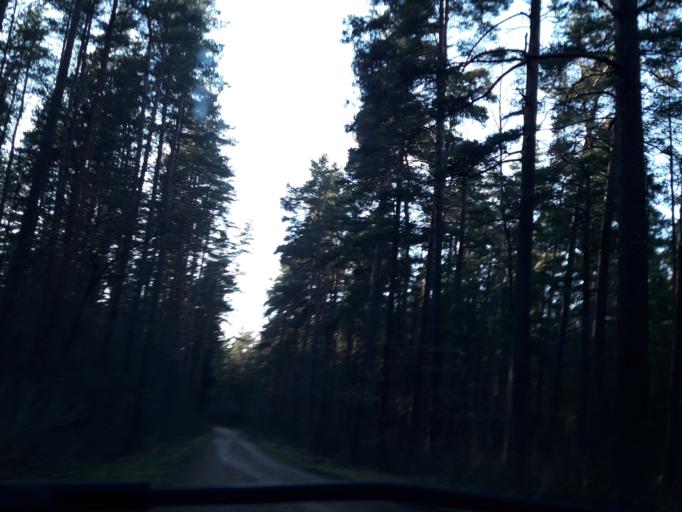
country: LV
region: Kekava
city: Kekava
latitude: 56.8609
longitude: 24.2276
